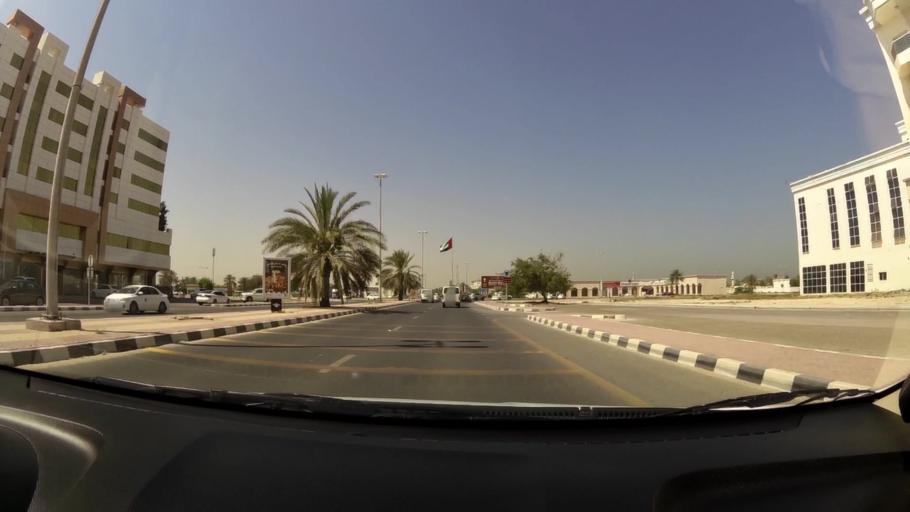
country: AE
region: Umm al Qaywayn
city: Umm al Qaywayn
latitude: 25.5669
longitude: 55.5541
